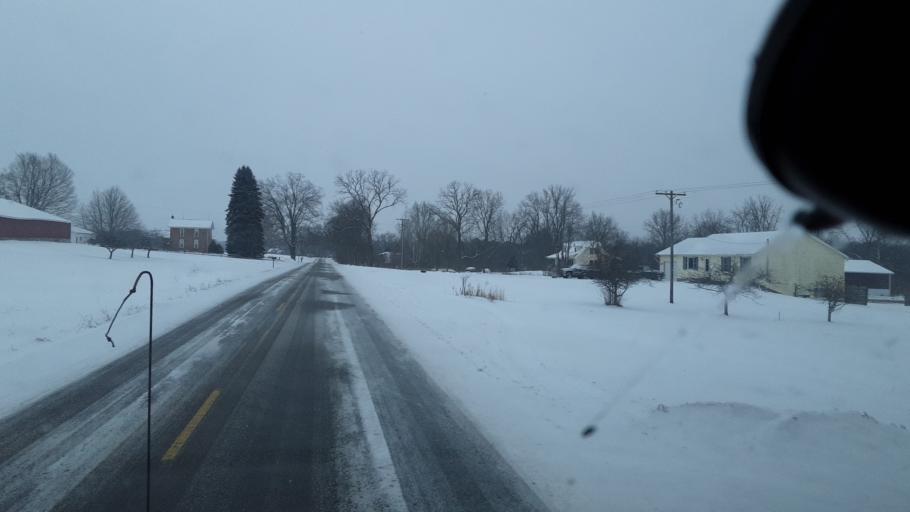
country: US
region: Michigan
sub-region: Ingham County
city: Leslie
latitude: 42.4302
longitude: -84.3168
